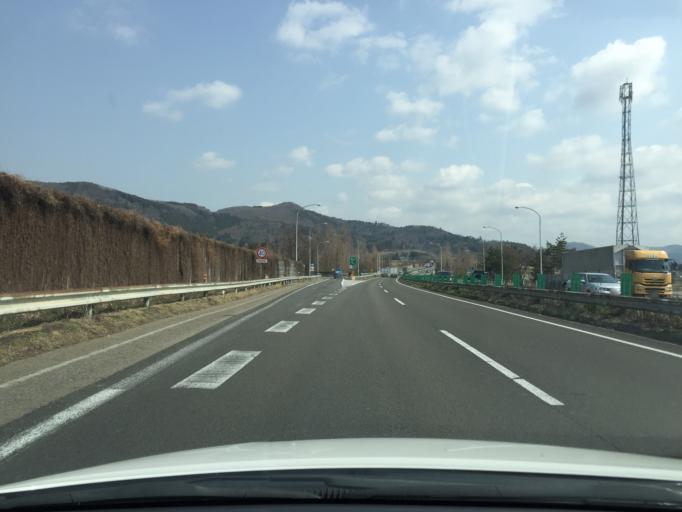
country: JP
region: Miyagi
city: Shiroishi
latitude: 38.0364
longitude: 140.6292
